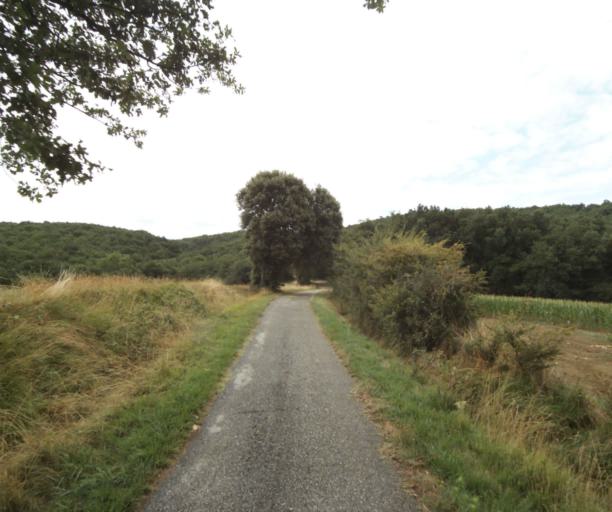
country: FR
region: Midi-Pyrenees
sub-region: Departement de la Haute-Garonne
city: Revel
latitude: 43.4154
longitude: 1.9815
